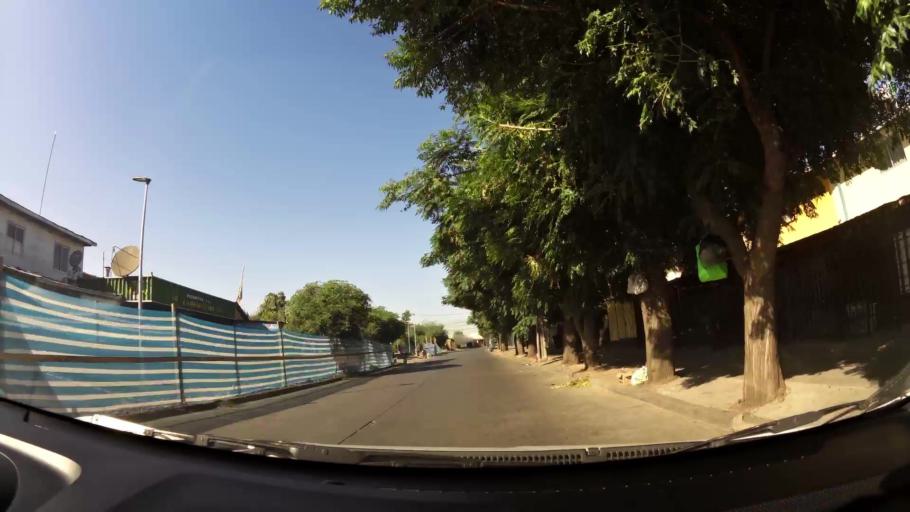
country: CL
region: Maule
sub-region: Provincia de Curico
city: Curico
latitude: -34.9955
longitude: -71.2570
